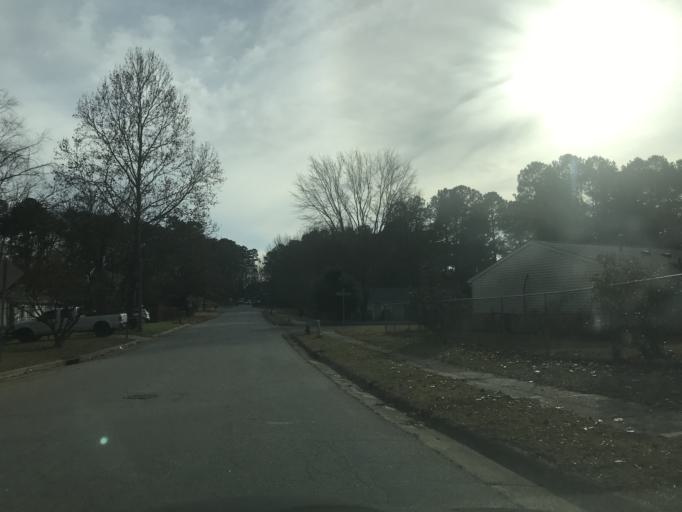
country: US
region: North Carolina
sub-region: Wake County
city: Raleigh
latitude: 35.8342
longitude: -78.5874
